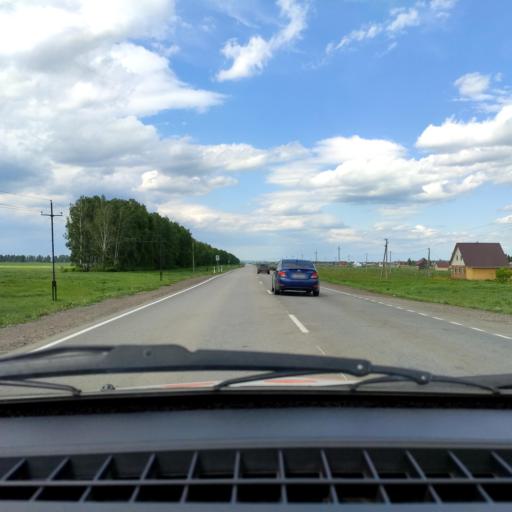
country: RU
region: Bashkortostan
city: Iglino
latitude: 54.9879
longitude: 56.5024
